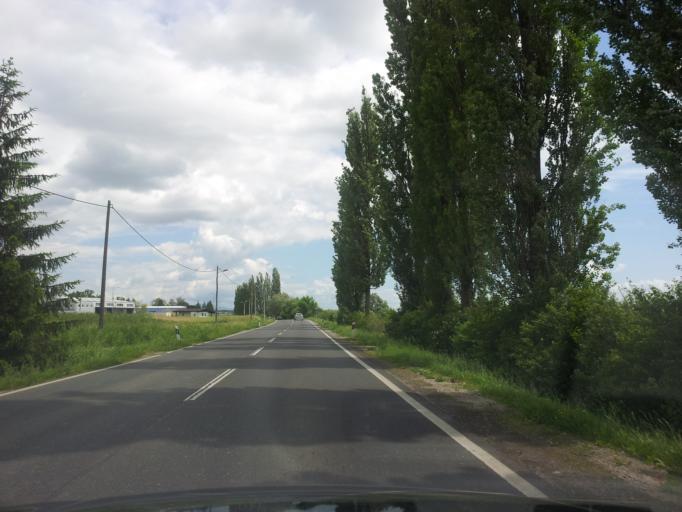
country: HR
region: Zagrebacka
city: Jastrebarsko
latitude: 45.6479
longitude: 15.6244
